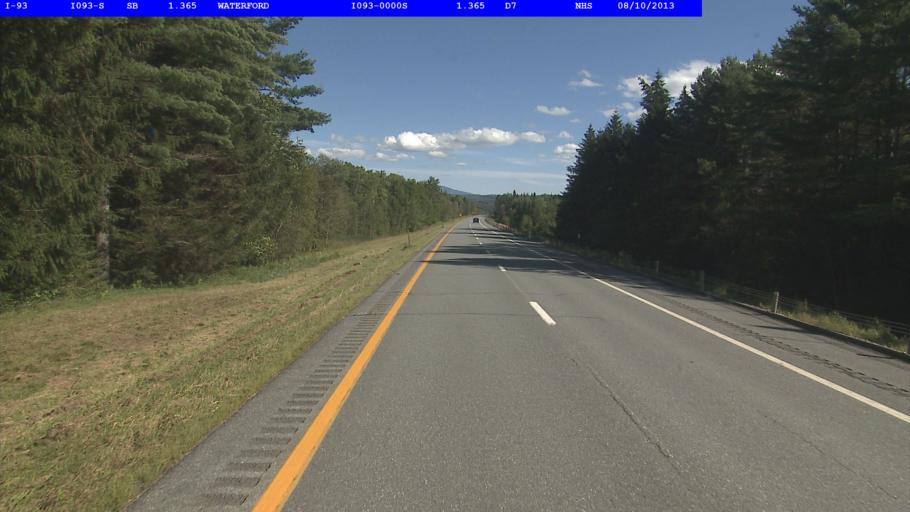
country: US
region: Vermont
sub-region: Caledonia County
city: Saint Johnsbury
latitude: 44.3619
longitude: -71.9003
